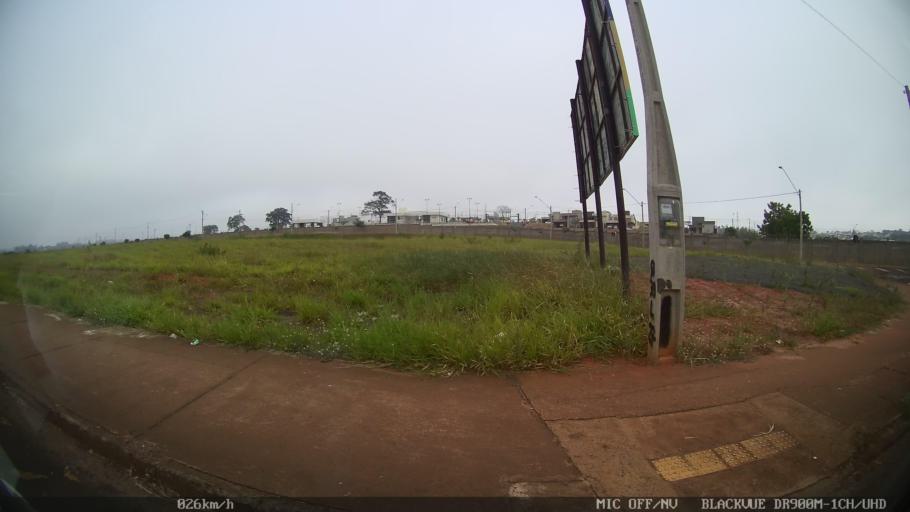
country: BR
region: Sao Paulo
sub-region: Sao Jose Do Rio Preto
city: Sao Jose do Rio Preto
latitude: -20.8518
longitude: -49.3705
